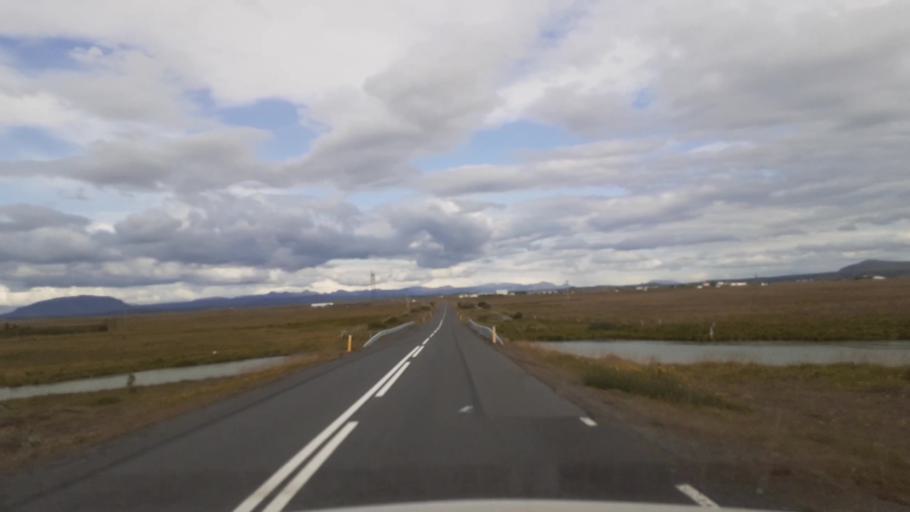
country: IS
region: South
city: Selfoss
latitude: 63.9347
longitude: -20.8413
